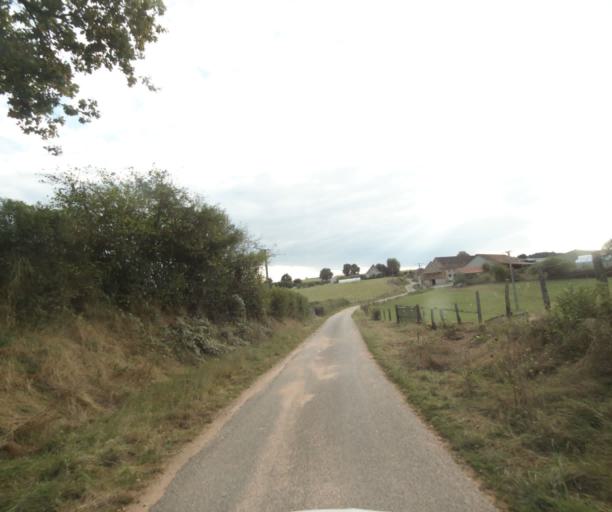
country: FR
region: Bourgogne
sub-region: Departement de Saone-et-Loire
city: Charolles
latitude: 46.4468
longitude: 4.3747
